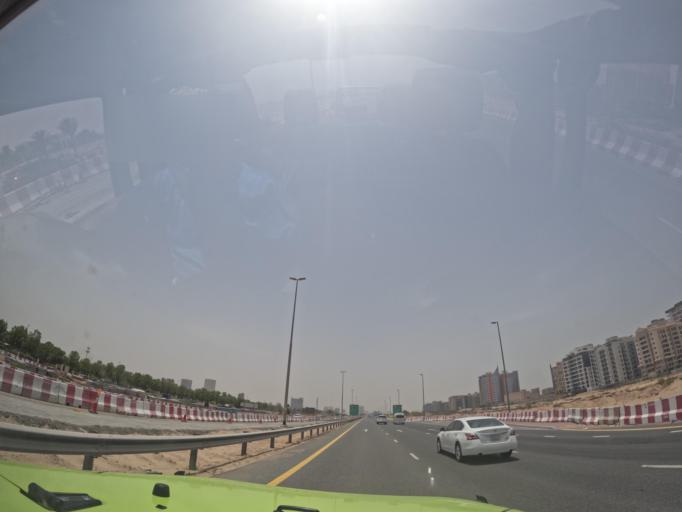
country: AE
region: Dubai
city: Dubai
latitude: 25.1126
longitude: 55.3908
